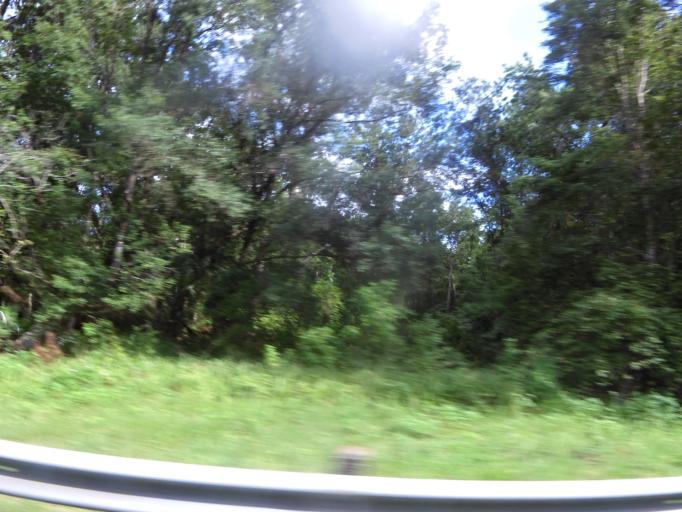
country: US
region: Florida
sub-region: Clay County
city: Green Cove Springs
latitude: 29.9262
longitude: -81.6785
